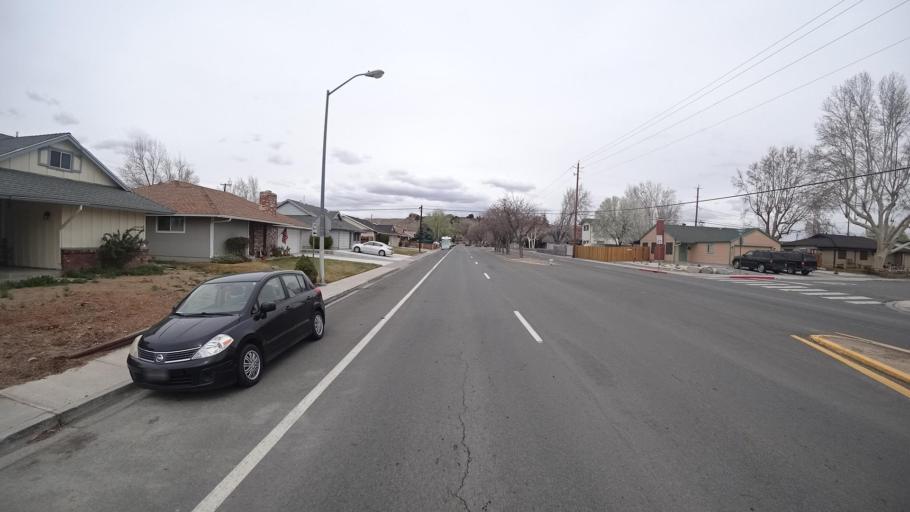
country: US
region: Nevada
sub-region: Washoe County
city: Sparks
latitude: 39.5535
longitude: -119.7620
